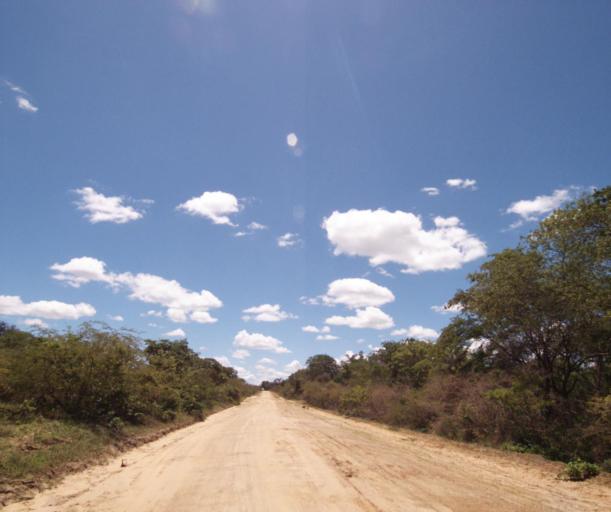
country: BR
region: Bahia
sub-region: Carinhanha
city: Carinhanha
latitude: -14.2101
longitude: -43.9813
